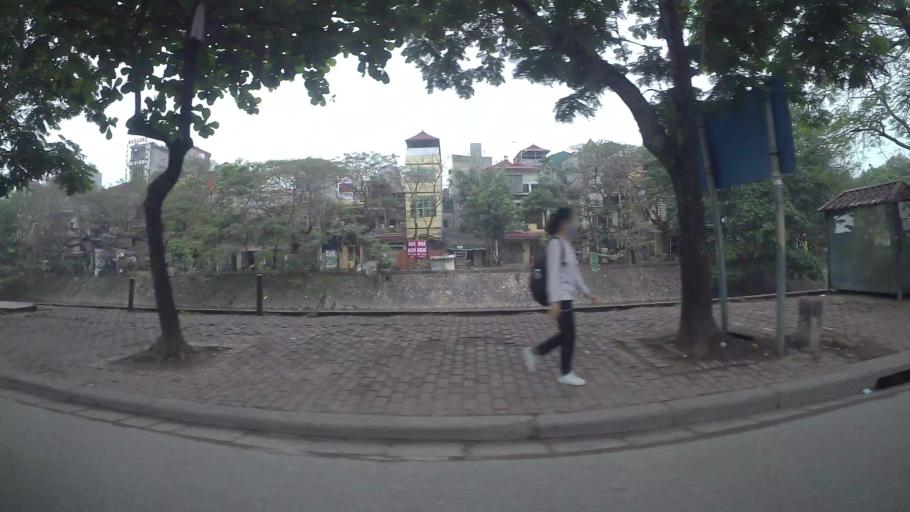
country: VN
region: Ha Noi
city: Hai BaTrung
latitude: 20.9877
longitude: 105.8633
